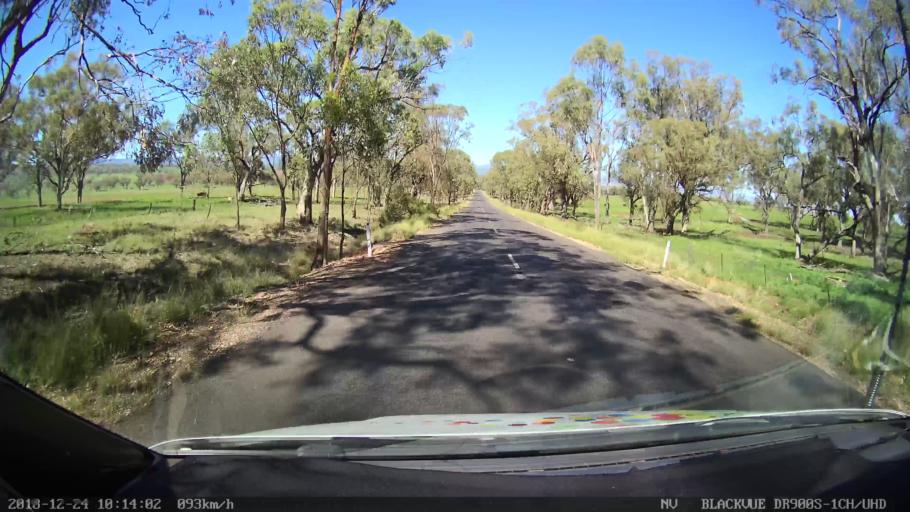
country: AU
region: New South Wales
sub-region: Liverpool Plains
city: Quirindi
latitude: -31.6947
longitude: 150.6337
